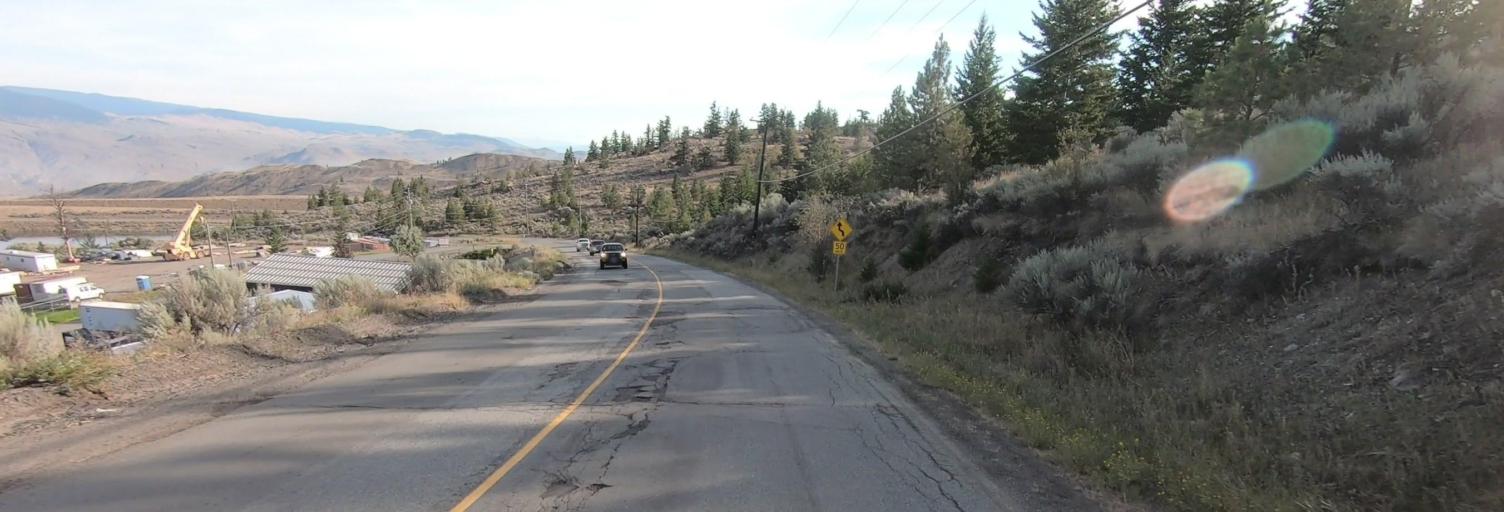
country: CA
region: British Columbia
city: Kamloops
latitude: 50.6582
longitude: -120.4359
